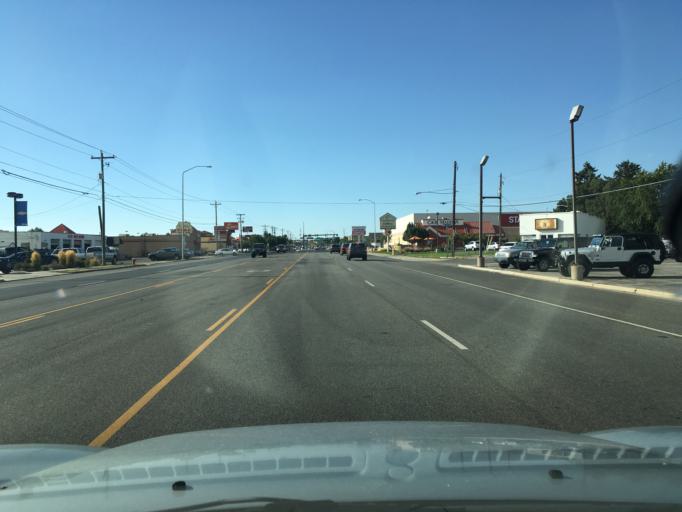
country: US
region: Utah
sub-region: Davis County
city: Layton
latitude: 41.0698
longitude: -111.9757
